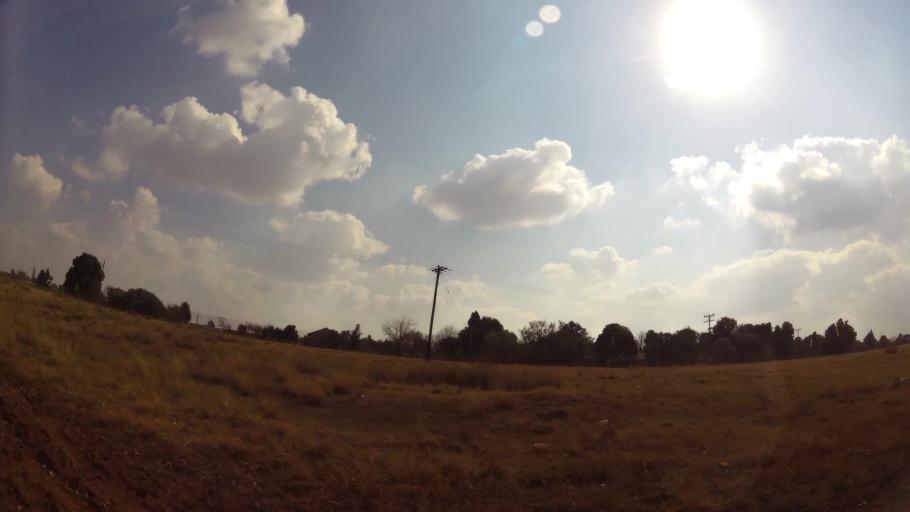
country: ZA
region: Mpumalanga
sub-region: Nkangala District Municipality
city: Delmas
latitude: -26.1561
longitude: 28.5567
